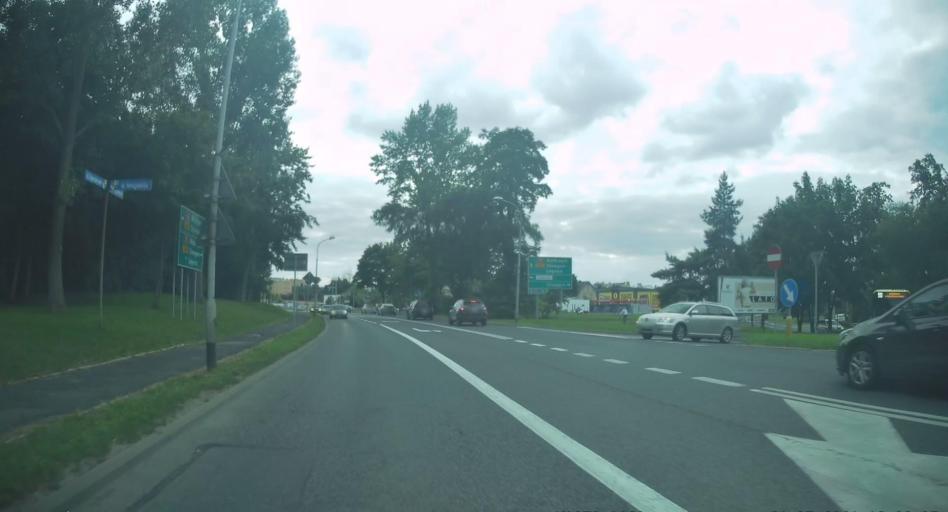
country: PL
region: Lower Silesian Voivodeship
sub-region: Powiat swidnicki
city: Swidnica
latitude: 50.8507
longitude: 16.4779
